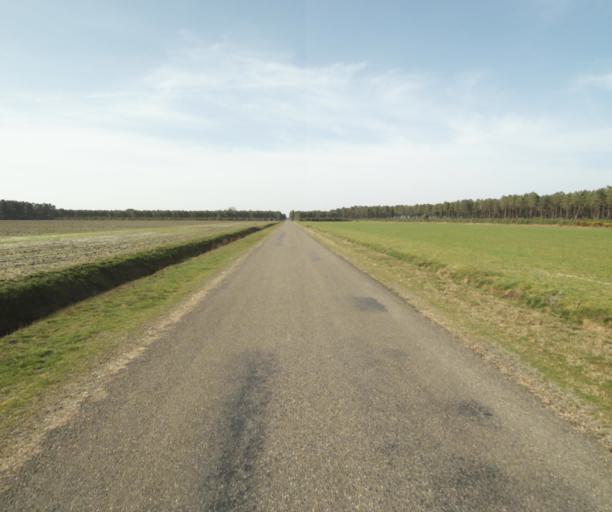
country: FR
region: Aquitaine
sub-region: Departement des Landes
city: Roquefort
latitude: 44.1789
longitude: -0.2062
